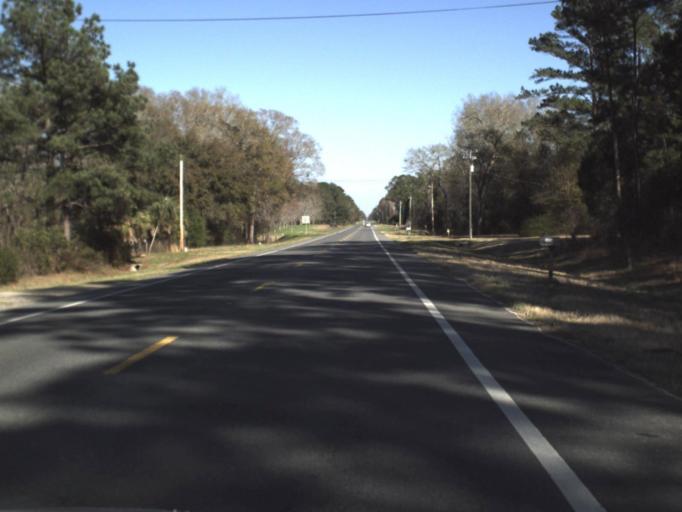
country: US
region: Florida
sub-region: Washington County
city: Chipley
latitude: 30.7871
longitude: -85.4392
